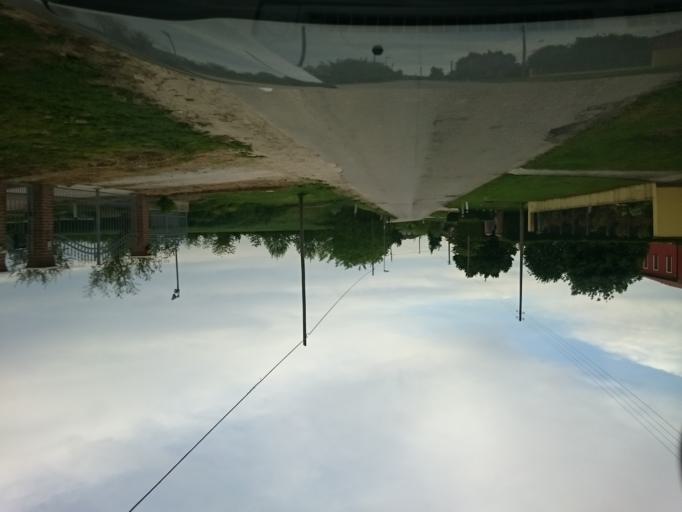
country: IT
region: Veneto
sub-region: Provincia di Padova
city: Cartura
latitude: 45.2842
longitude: 11.8438
